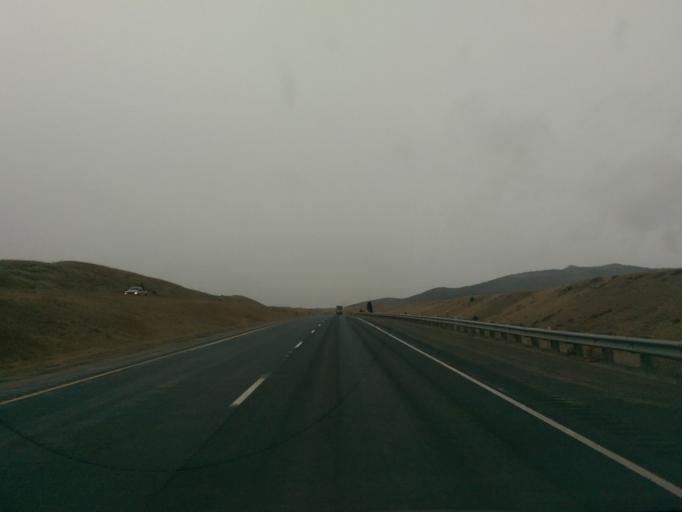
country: US
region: Montana
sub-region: Gallatin County
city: Three Forks
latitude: 45.8986
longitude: -111.8252
